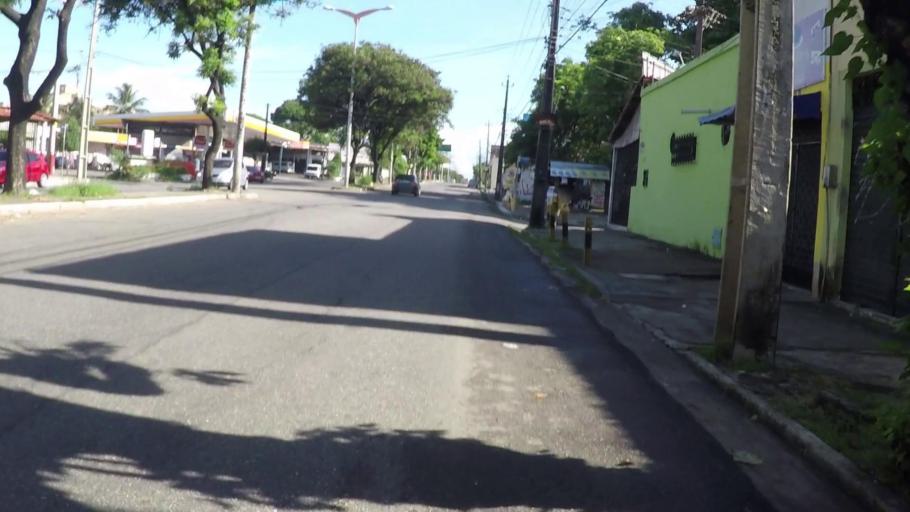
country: BR
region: Ceara
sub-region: Fortaleza
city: Fortaleza
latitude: -3.7109
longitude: -38.5895
